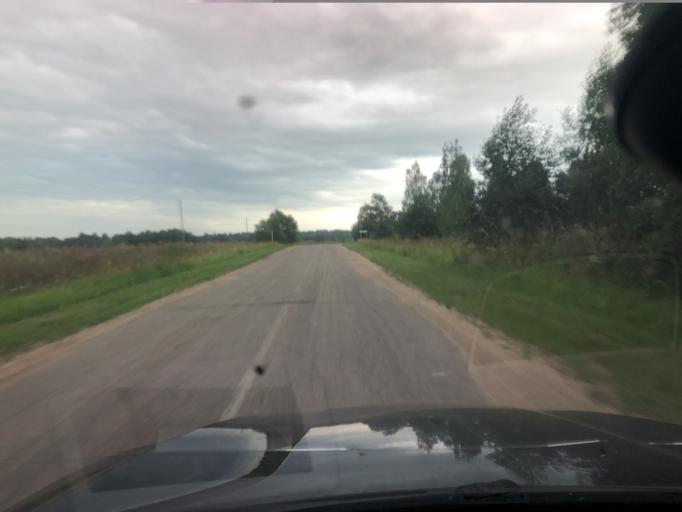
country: RU
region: Jaroslavl
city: Pereslavl'-Zalesskiy
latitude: 57.0322
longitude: 38.9114
